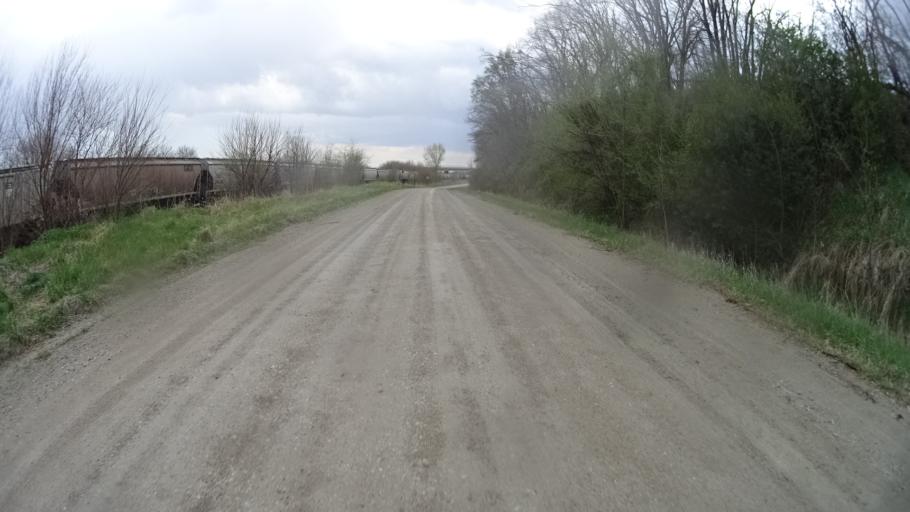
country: US
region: Nebraska
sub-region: Sarpy County
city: Offutt Air Force Base
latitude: 41.0849
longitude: -95.9165
